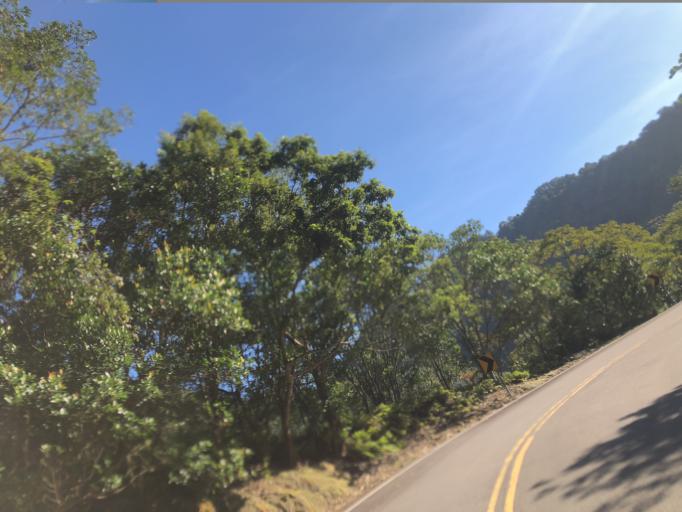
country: TW
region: Taiwan
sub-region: Miaoli
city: Miaoli
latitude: 24.5857
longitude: 120.9274
